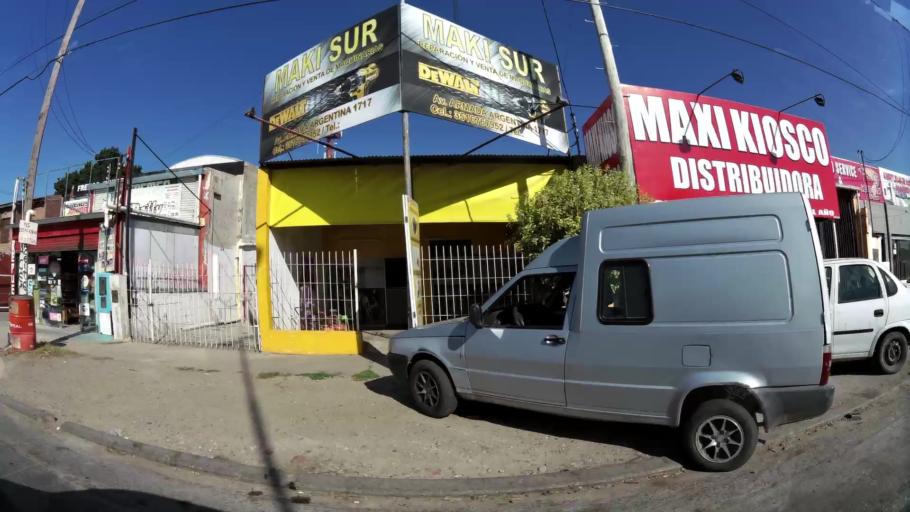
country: AR
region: Cordoba
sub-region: Departamento de Capital
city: Cordoba
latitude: -31.4687
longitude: -64.2262
